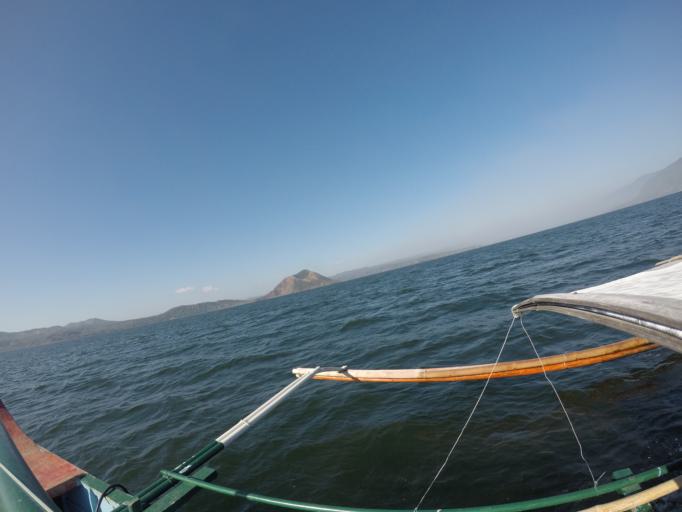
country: PH
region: Calabarzon
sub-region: Province of Batangas
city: Sampaloc
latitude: 14.0616
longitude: 120.9952
